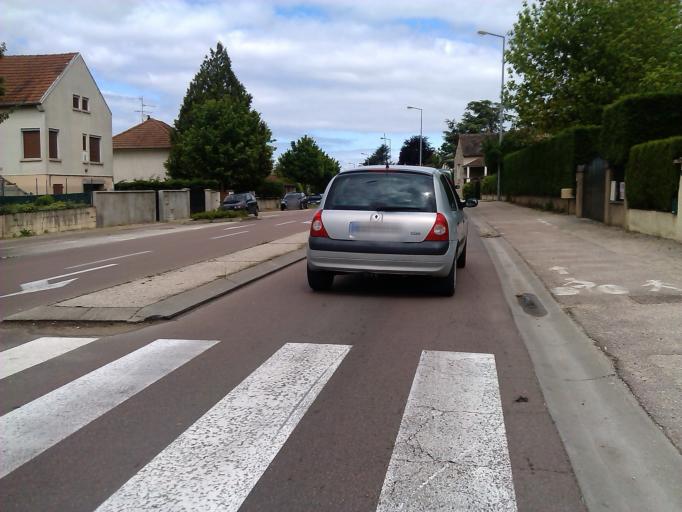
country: FR
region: Bourgogne
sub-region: Departement de Saone-et-Loire
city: Champforgeuil
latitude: 46.8142
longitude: 4.8416
